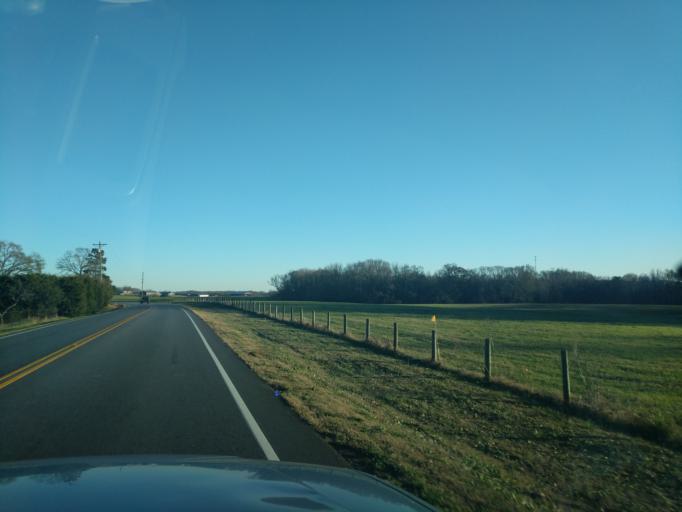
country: US
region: South Carolina
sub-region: Oconee County
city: Utica
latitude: 34.5864
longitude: -82.9485
